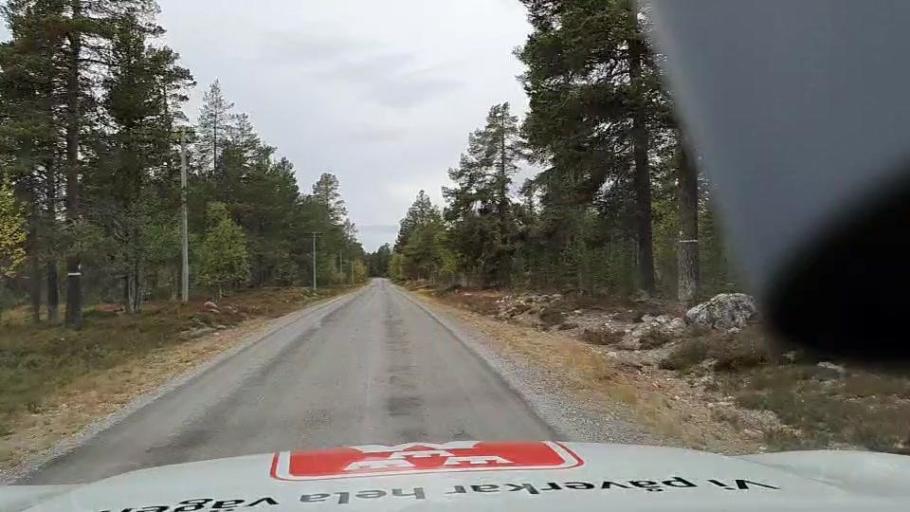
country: NO
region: Hedmark
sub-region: Engerdal
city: Engerdal
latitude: 62.0922
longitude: 12.7829
